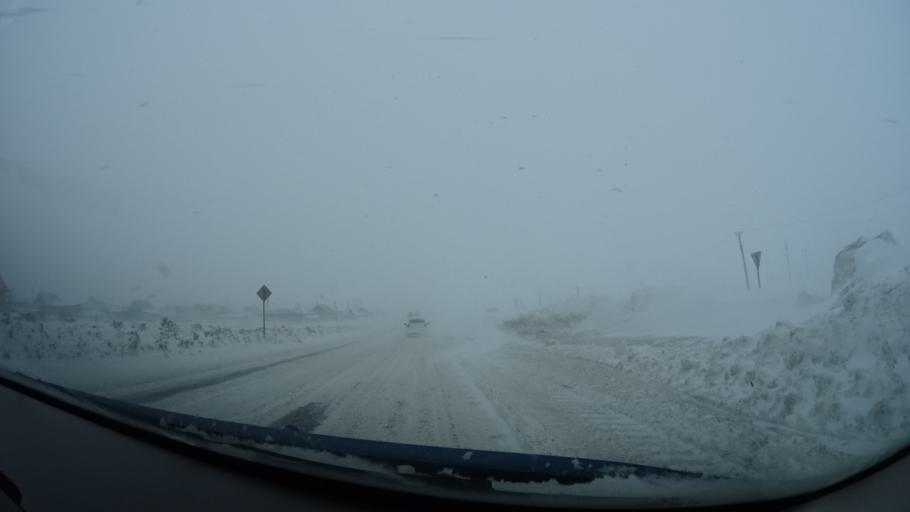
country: RU
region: Perm
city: Kuyeda
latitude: 56.4210
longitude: 55.5854
